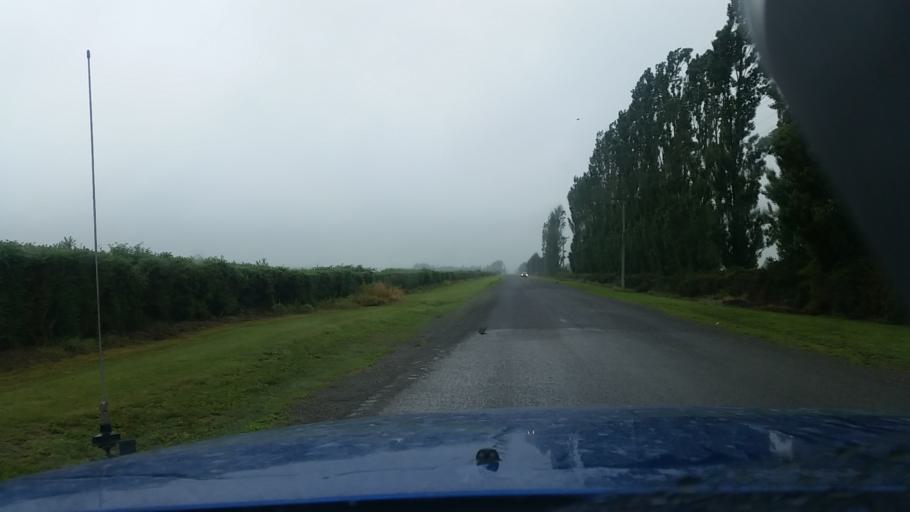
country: NZ
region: Canterbury
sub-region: Ashburton District
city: Rakaia
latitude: -43.7656
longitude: 171.8462
